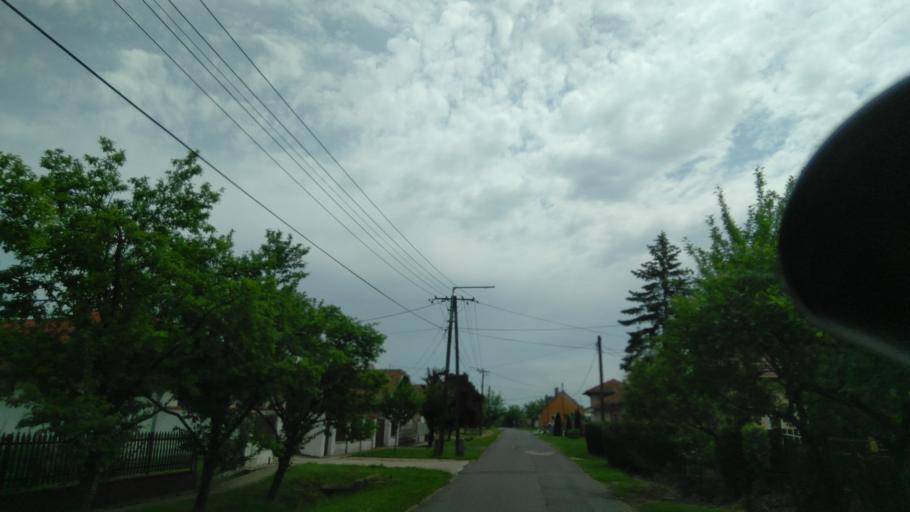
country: HU
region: Bekes
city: Fuzesgyarmat
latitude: 47.0995
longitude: 21.2103
